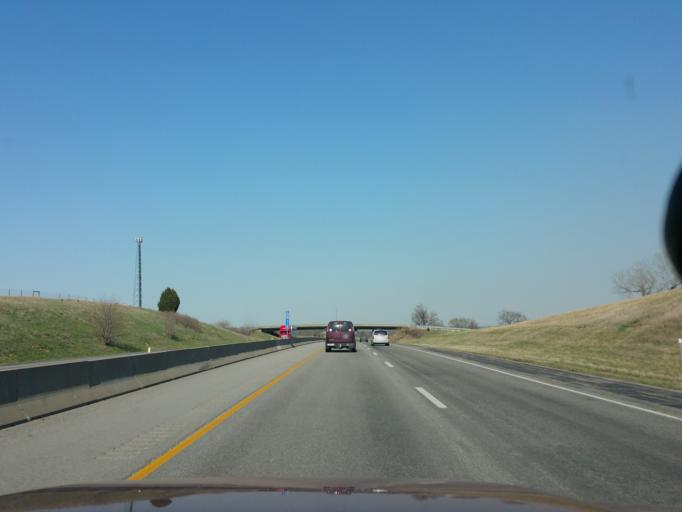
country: US
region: Kansas
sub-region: Leavenworth County
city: Tonganoxie
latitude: 39.0501
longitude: -95.0780
